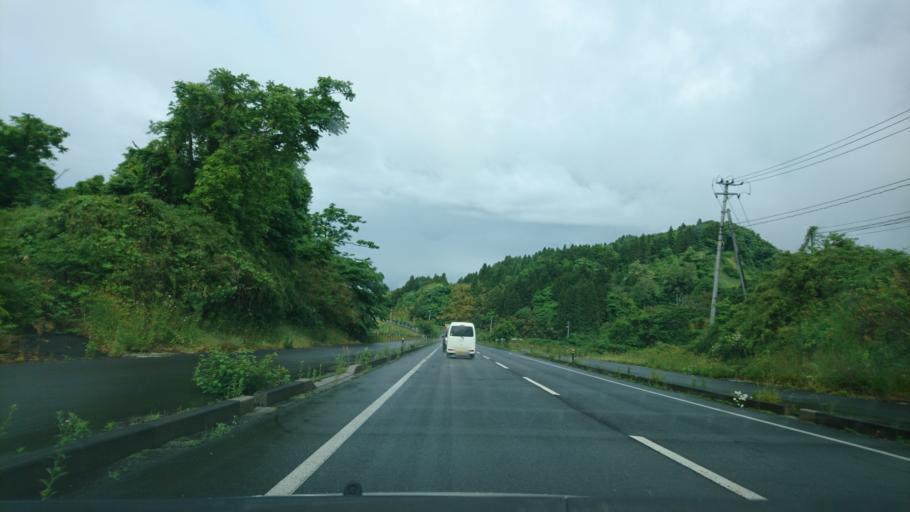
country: JP
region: Iwate
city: Ichinoseki
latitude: 38.9412
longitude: 141.0810
